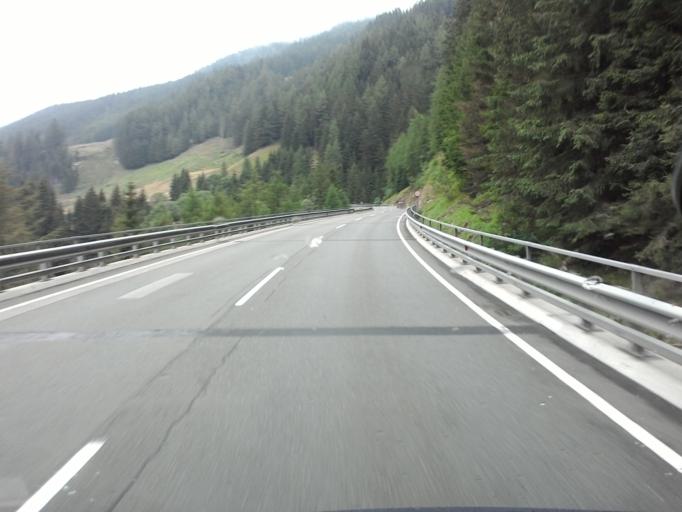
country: AT
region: Tyrol
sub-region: Politischer Bezirk Lienz
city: Matrei in Osttirol
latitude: 47.0862
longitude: 12.5305
